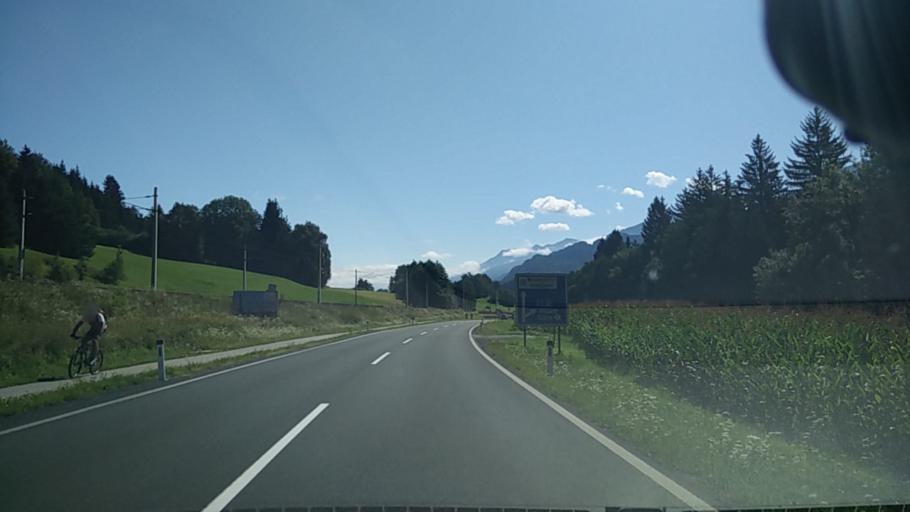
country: AT
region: Carinthia
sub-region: Politischer Bezirk Villach Land
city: Hohenthurn
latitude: 46.5515
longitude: 13.6721
